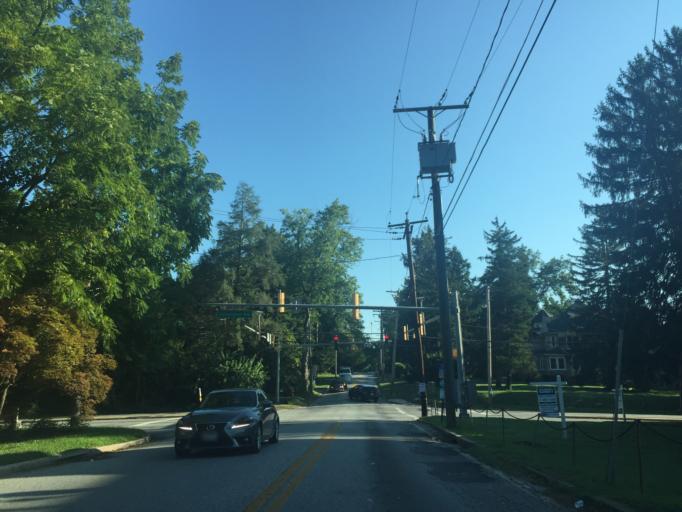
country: US
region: Maryland
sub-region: Howard County
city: Ilchester
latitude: 39.2733
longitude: -76.7566
